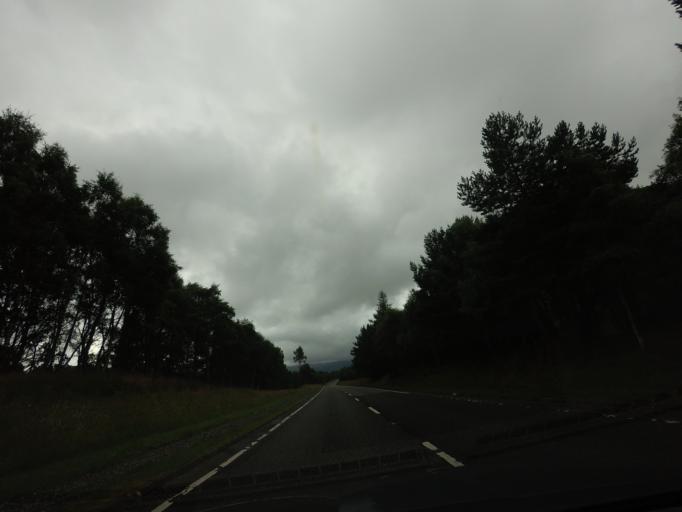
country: GB
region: Scotland
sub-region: Highland
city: Aviemore
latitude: 57.1878
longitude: -3.8365
